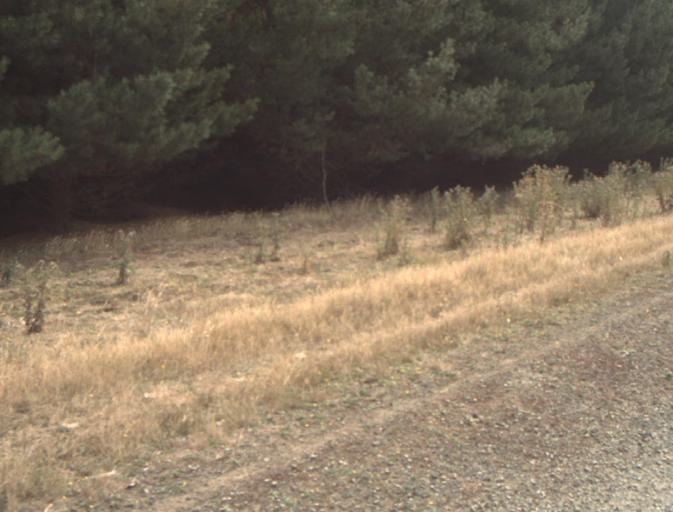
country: AU
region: Tasmania
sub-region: Dorset
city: Scottsdale
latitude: -41.4678
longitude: 147.6025
